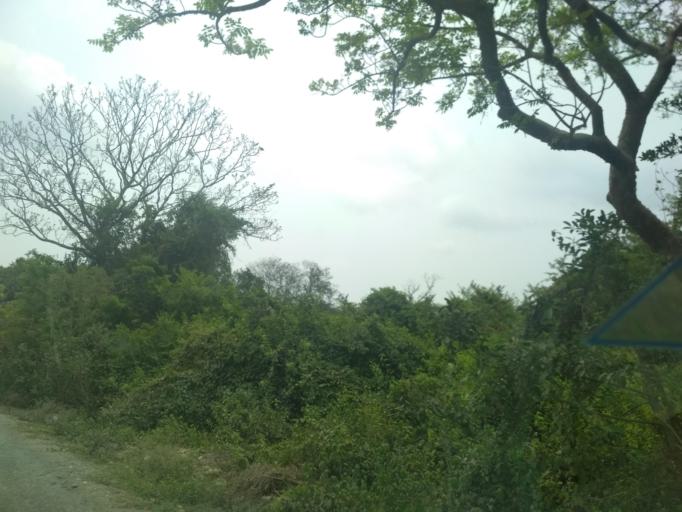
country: MX
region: Veracruz
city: Paso del Toro
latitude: 19.0410
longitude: -96.1498
